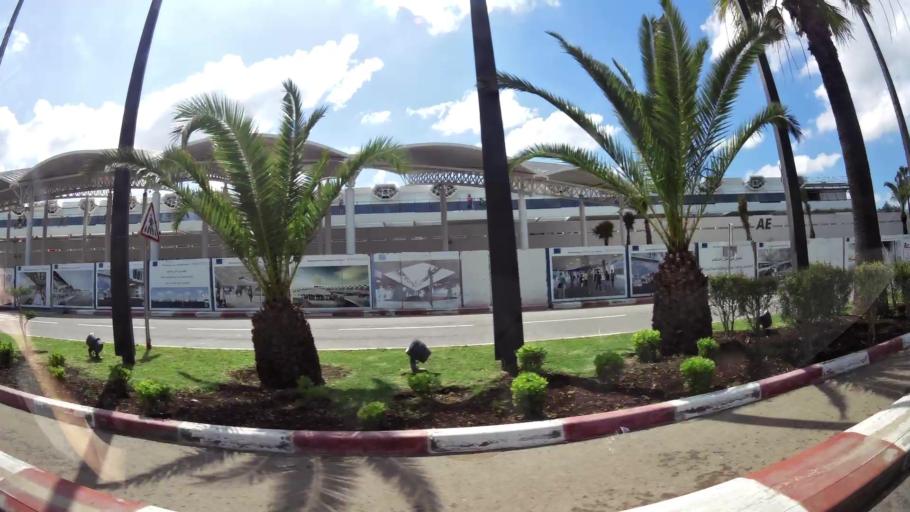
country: MA
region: Chaouia-Ouardigha
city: Nouaseur
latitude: 33.3748
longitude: -7.5805
